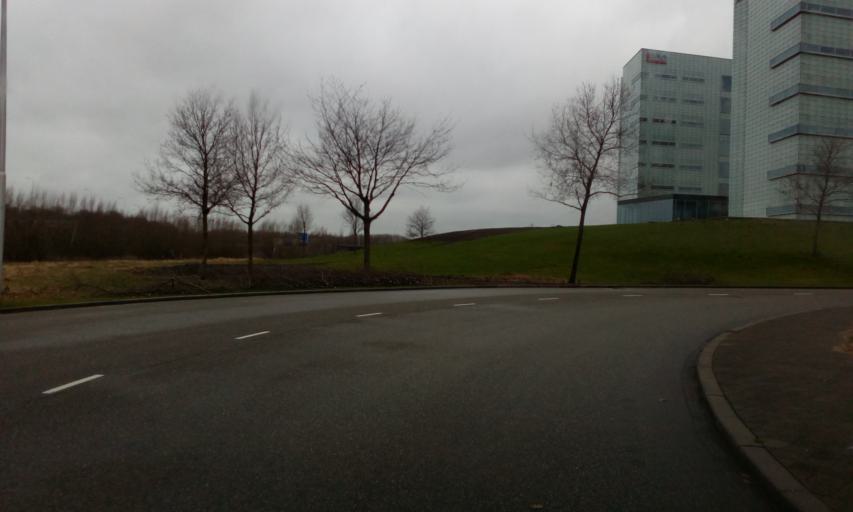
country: NL
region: Utrecht
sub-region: Gemeente Nieuwegein
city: Nieuwegein
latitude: 52.0661
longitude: 5.0764
